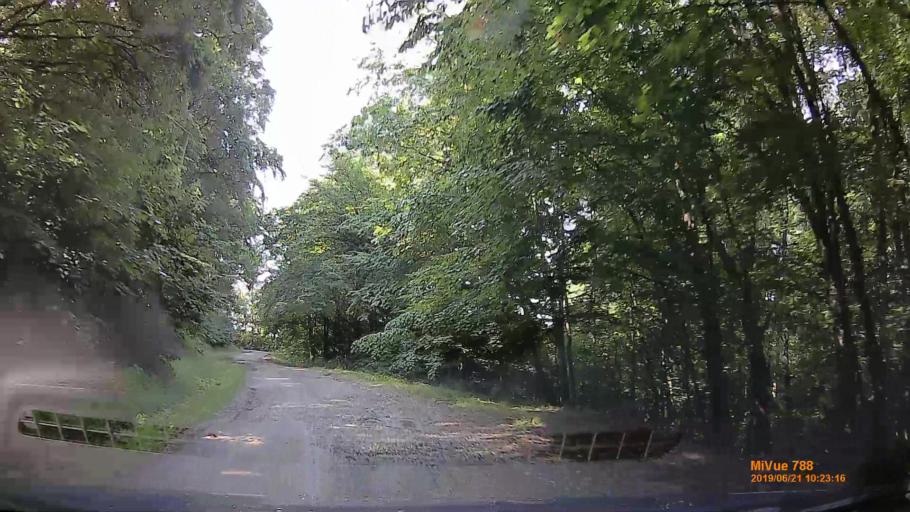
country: HU
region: Baranya
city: Buekkoesd
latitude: 46.1870
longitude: 17.9702
